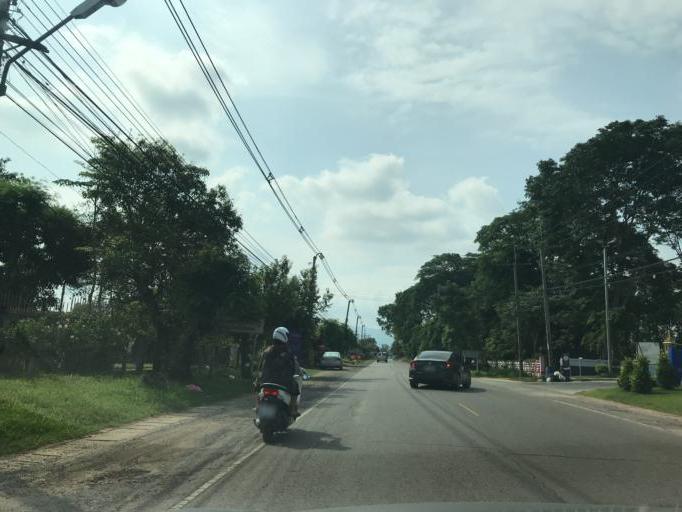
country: TH
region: Phayao
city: Chiang Kham
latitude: 19.5165
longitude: 100.3131
